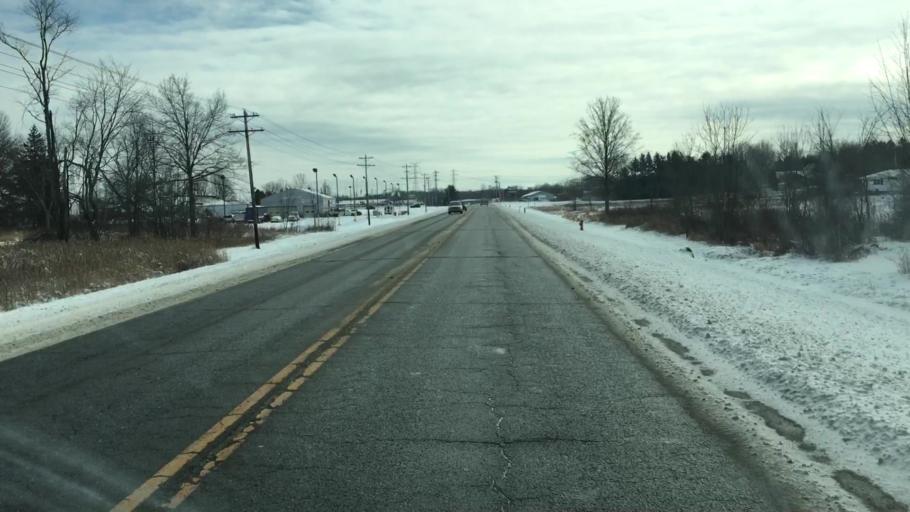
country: US
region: Ohio
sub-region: Columbiana County
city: Columbiana
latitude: 40.8929
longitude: -80.6768
